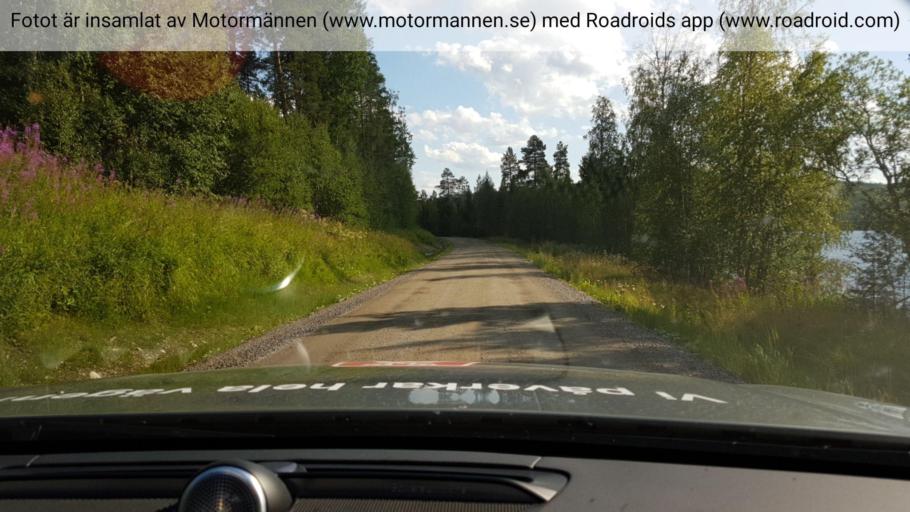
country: SE
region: Jaemtland
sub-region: Stroemsunds Kommun
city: Stroemsund
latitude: 64.0038
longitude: 15.9677
